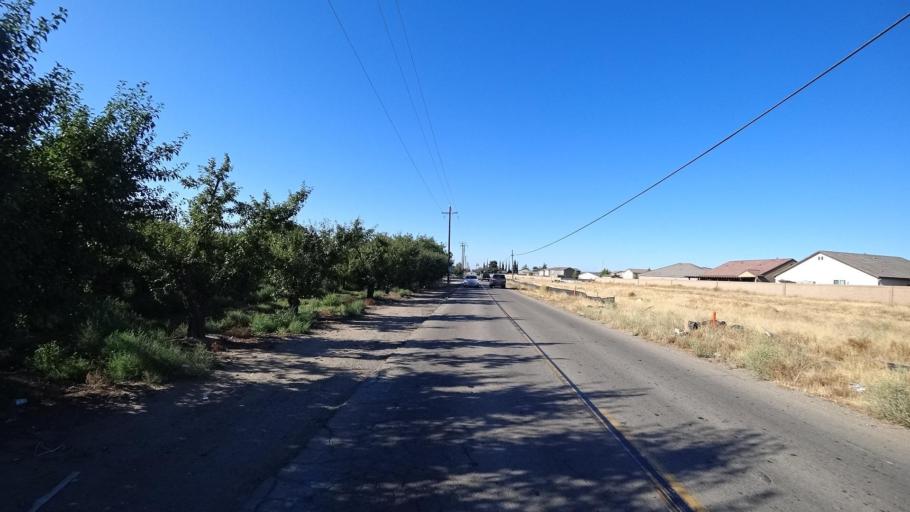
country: US
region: California
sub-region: Fresno County
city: Sunnyside
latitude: 36.7219
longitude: -119.6641
